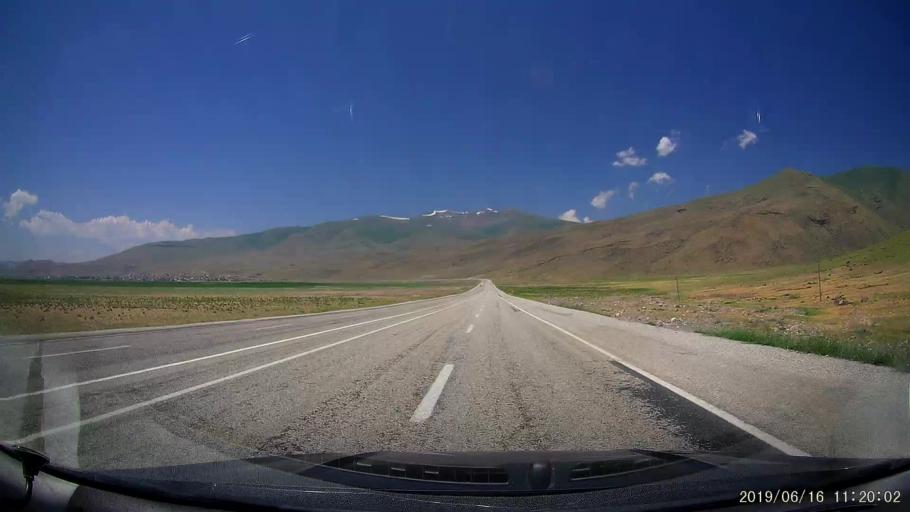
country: TR
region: Agri
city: Dogubayazit
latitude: 39.6966
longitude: 44.1010
